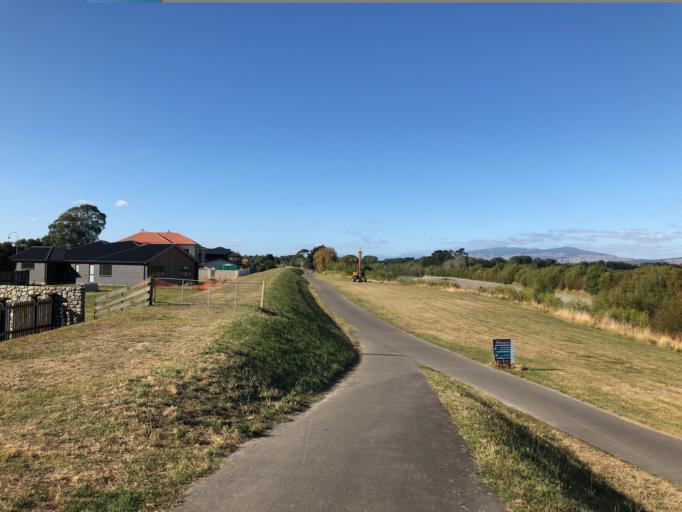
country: NZ
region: Manawatu-Wanganui
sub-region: Palmerston North City
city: Palmerston North
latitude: -40.3728
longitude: 175.6415
